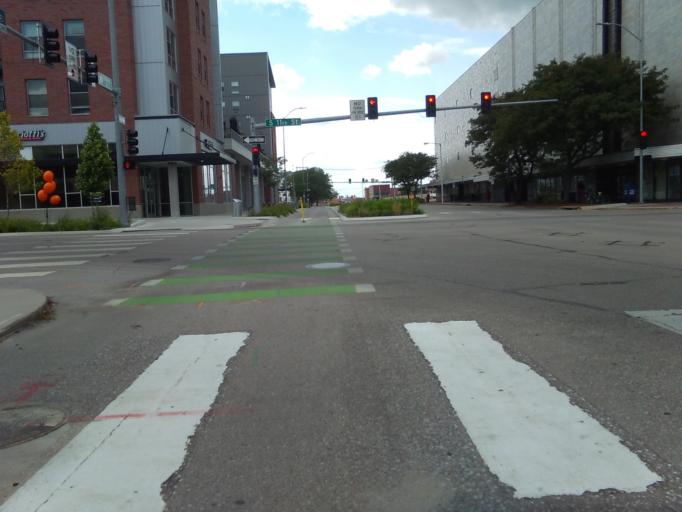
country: US
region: Nebraska
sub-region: Lancaster County
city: Lincoln
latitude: 40.8124
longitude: -96.7054
